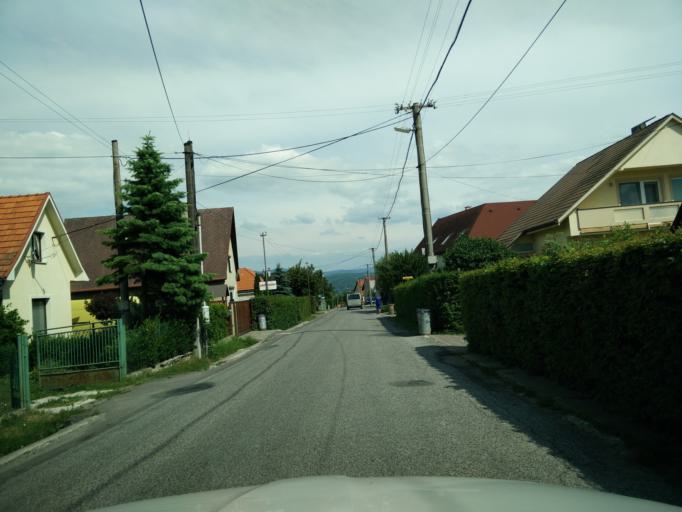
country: SK
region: Nitriansky
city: Bojnice
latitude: 48.8273
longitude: 18.6009
